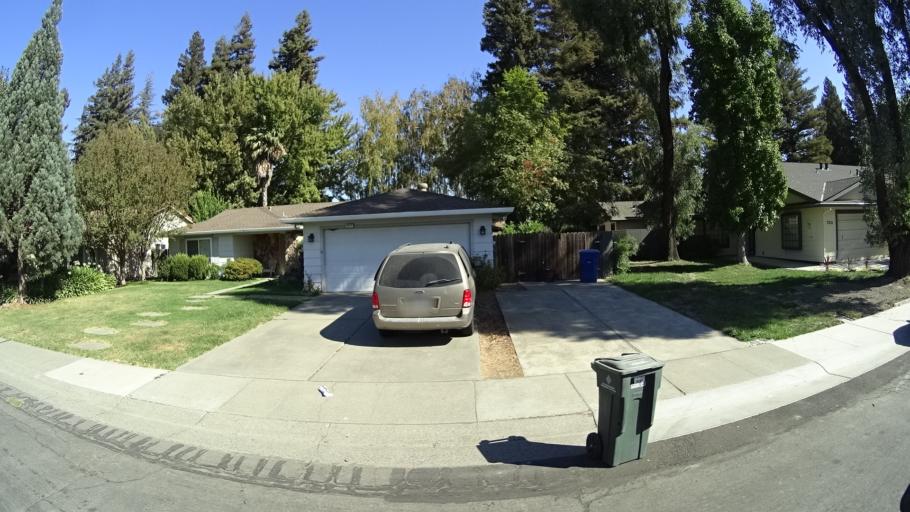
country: US
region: California
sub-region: Sacramento County
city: Parkway
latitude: 38.4949
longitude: -121.5266
